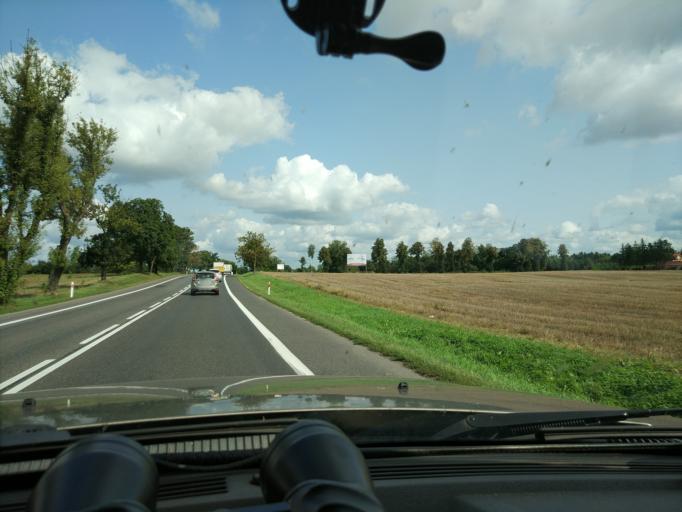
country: PL
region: Masovian Voivodeship
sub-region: Powiat mlawski
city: Wisniewo
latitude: 53.0794
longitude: 20.3546
